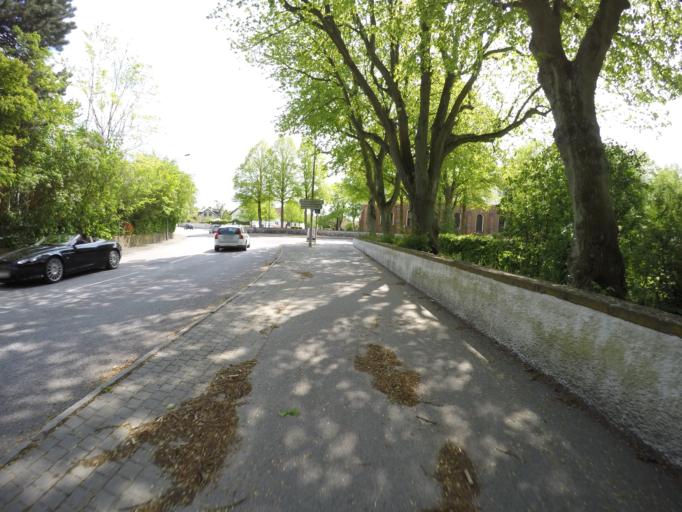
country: SE
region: Skane
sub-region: Malmo
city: Tygelsjo
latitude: 55.5287
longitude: 12.9952
